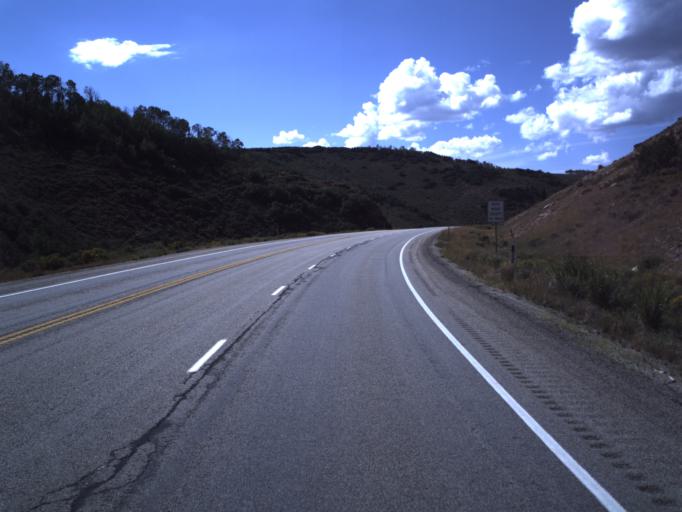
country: US
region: Utah
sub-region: Carbon County
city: Helper
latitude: 40.1928
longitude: -110.9590
